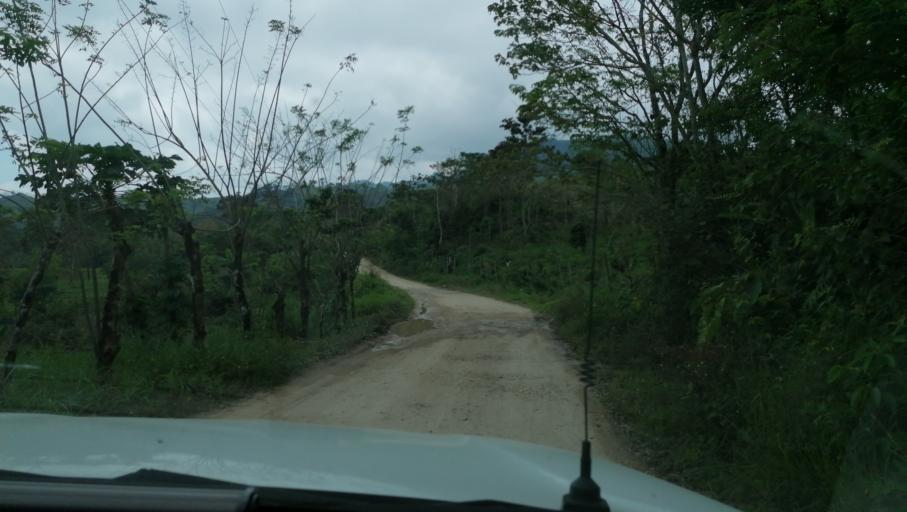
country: MX
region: Chiapas
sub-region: Ocotepec
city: San Pablo Huacano
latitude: 17.2752
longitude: -93.2345
